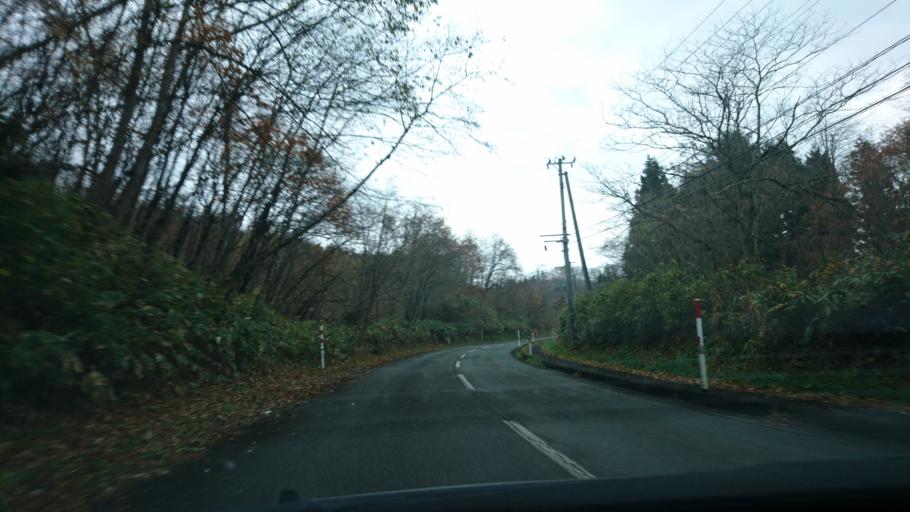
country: JP
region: Iwate
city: Ichinoseki
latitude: 38.9663
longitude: 140.9390
